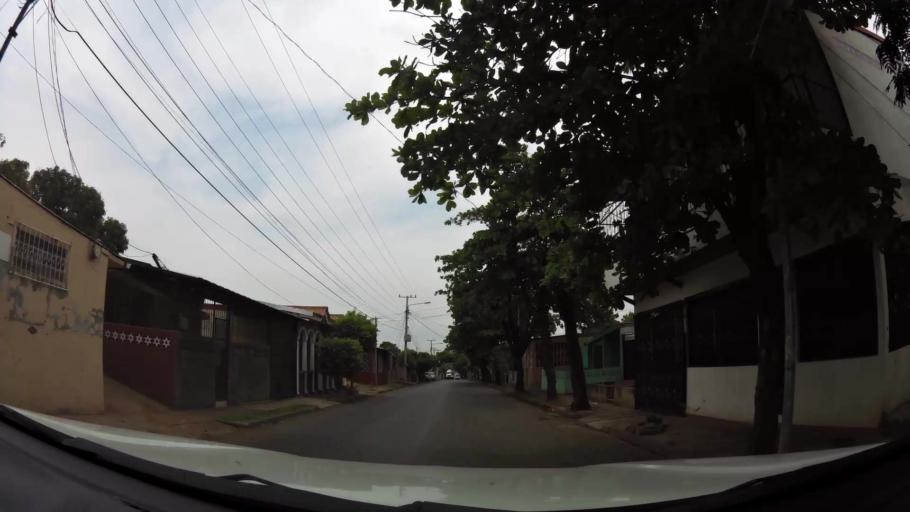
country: NI
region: Managua
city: Managua
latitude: 12.1206
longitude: -86.2291
